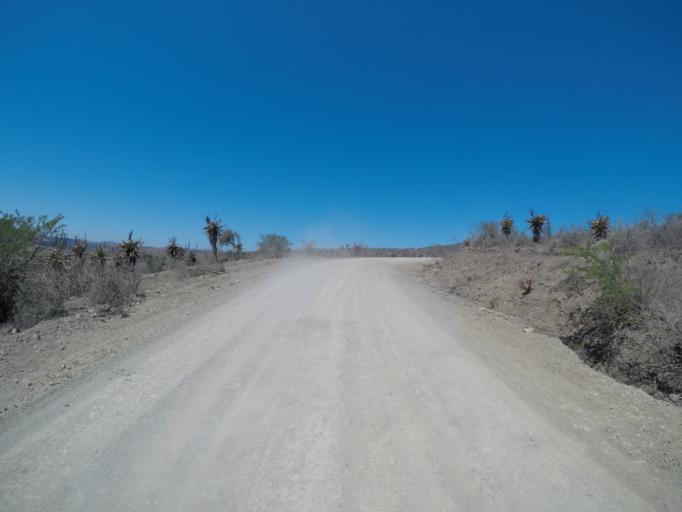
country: ZA
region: Eastern Cape
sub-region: OR Tambo District Municipality
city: Mthatha
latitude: -31.8729
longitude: 28.8721
